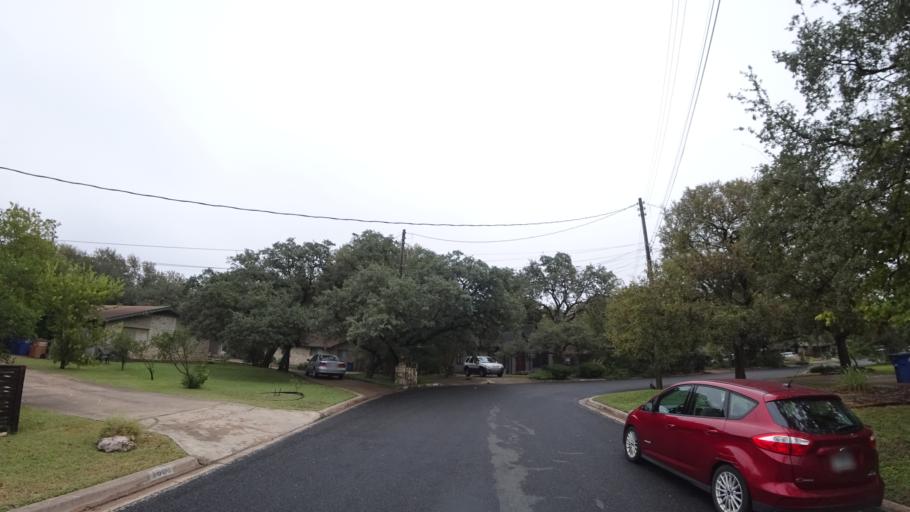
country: US
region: Texas
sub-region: Travis County
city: Rollingwood
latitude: 30.2568
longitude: -97.7747
